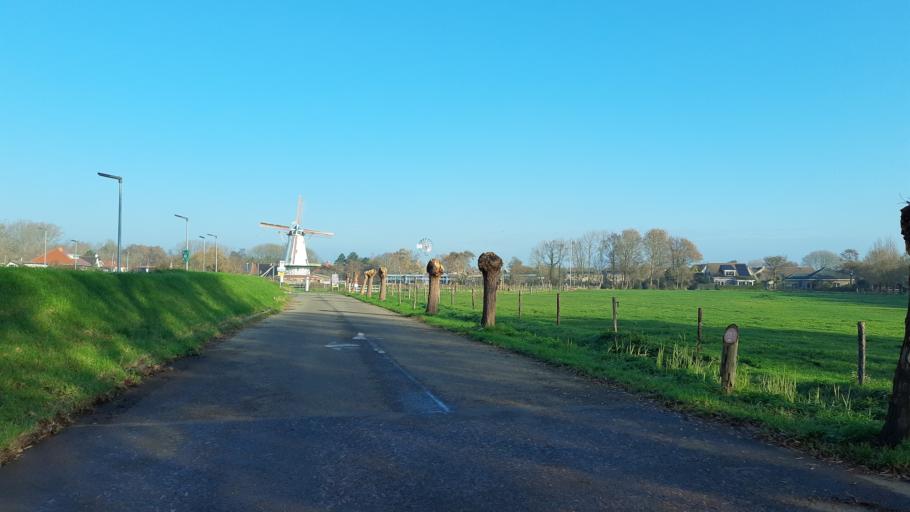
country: NL
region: Zeeland
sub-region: Schouwen-Duiveland
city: Burgh
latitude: 51.6917
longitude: 3.7365
